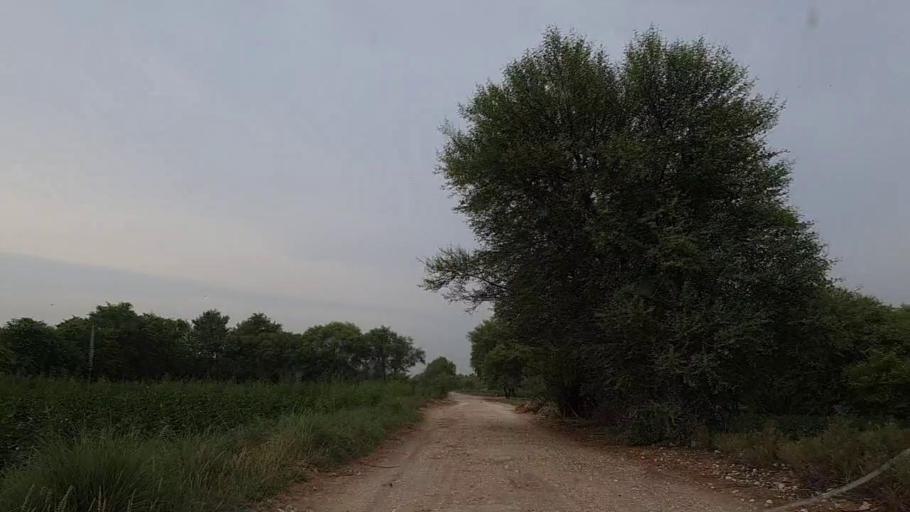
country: PK
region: Sindh
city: Khanpur
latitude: 27.8290
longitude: 69.6106
